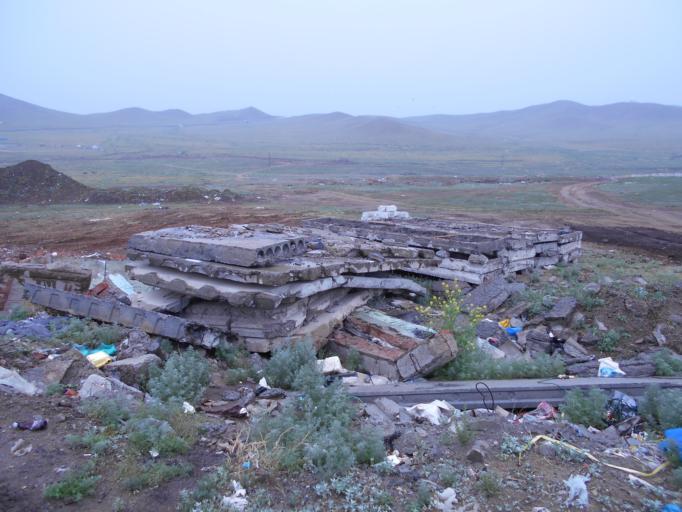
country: MN
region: Ulaanbaatar
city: Ulaanbaatar
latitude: 47.9178
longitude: 106.9148
